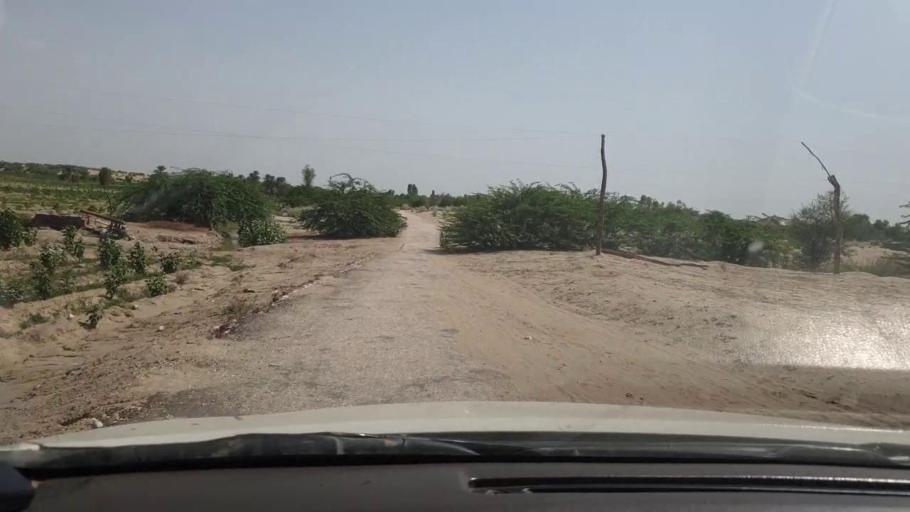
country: PK
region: Sindh
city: Rohri
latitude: 27.4667
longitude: 69.0789
